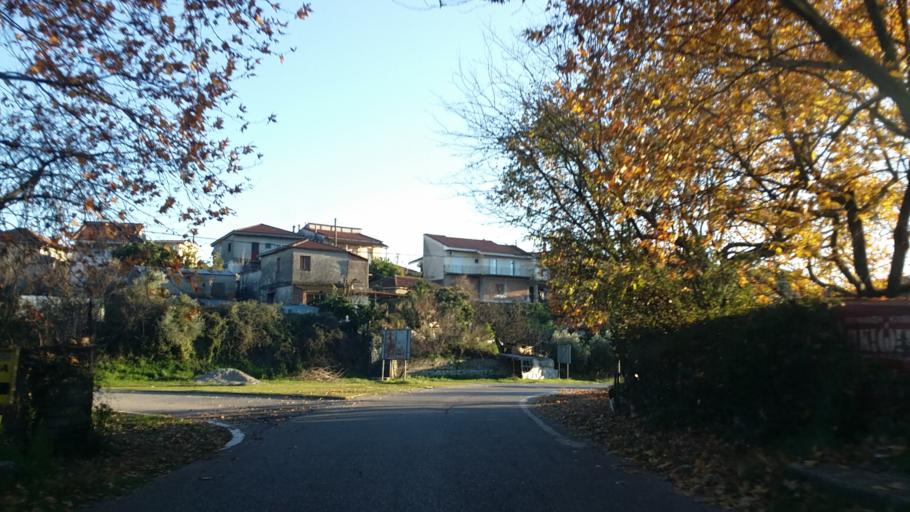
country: GR
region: West Greece
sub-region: Nomos Aitolias kai Akarnanias
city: Lepenou
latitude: 38.7395
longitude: 21.3461
